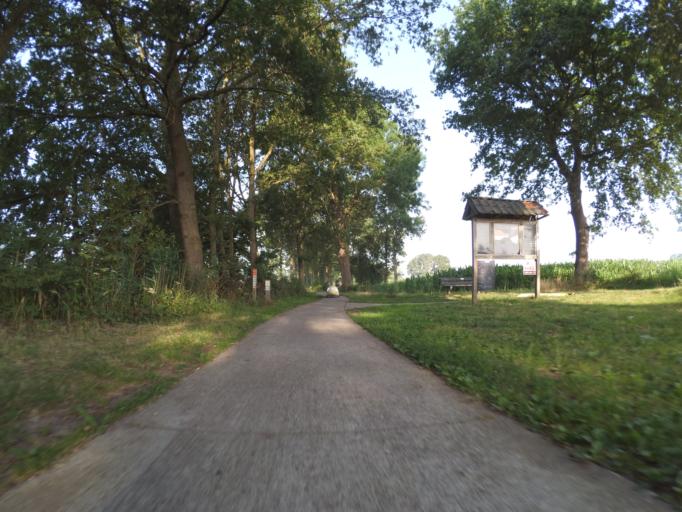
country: NL
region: Overijssel
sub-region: Gemeente Wierden
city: Wierden
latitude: 52.3191
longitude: 6.5665
